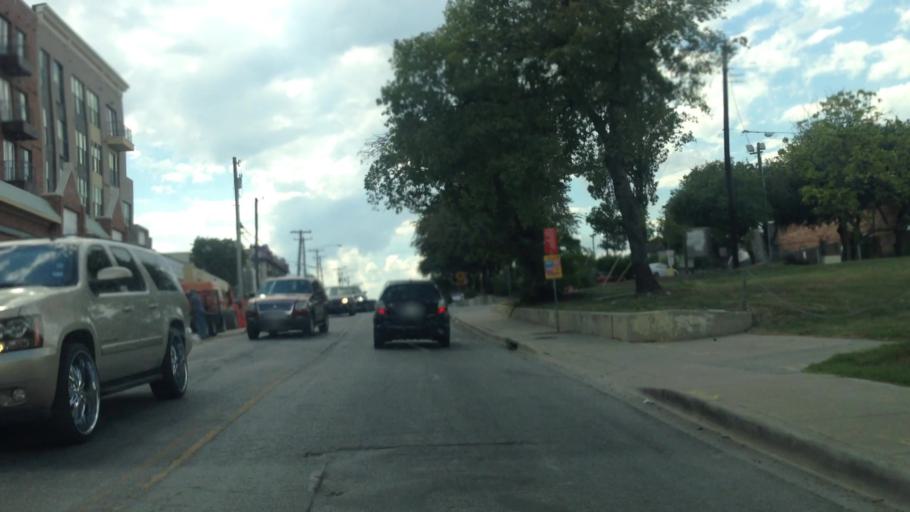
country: US
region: Texas
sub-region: Dallas County
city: Dallas
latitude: 32.7495
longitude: -96.8247
